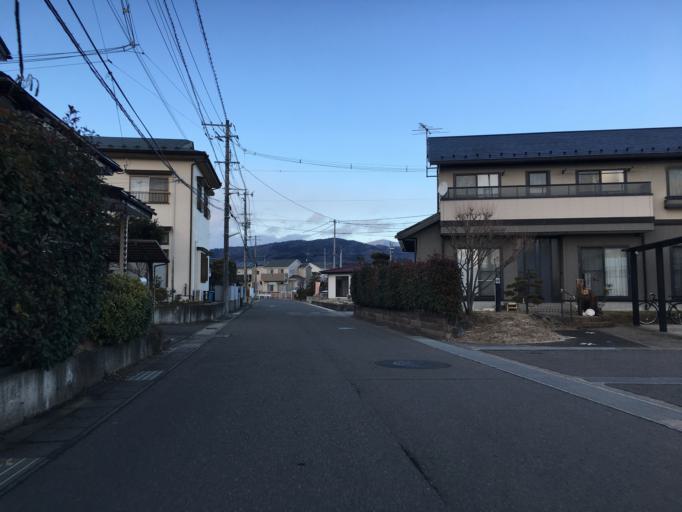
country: JP
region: Fukushima
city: Hobaramachi
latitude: 37.8095
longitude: 140.4895
